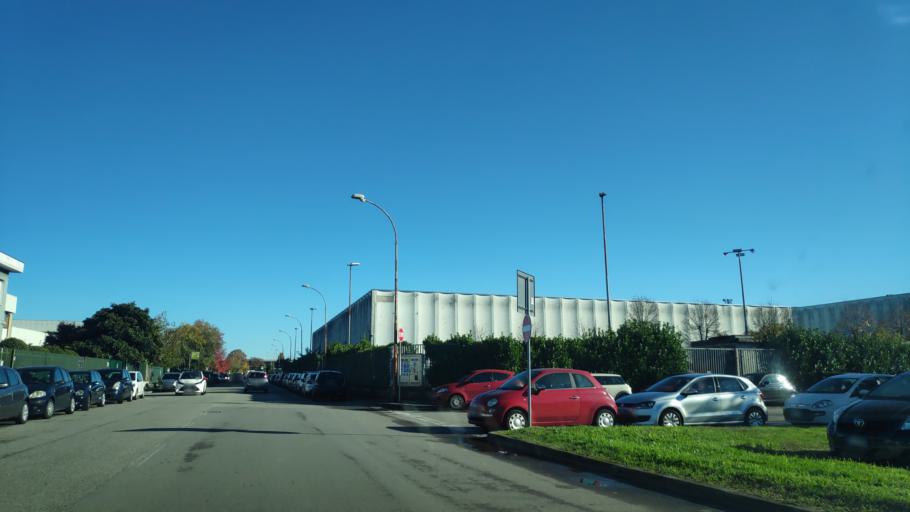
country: IT
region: Lombardy
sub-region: Citta metropolitana di Milano
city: Rozzano
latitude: 45.3735
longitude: 9.1731
